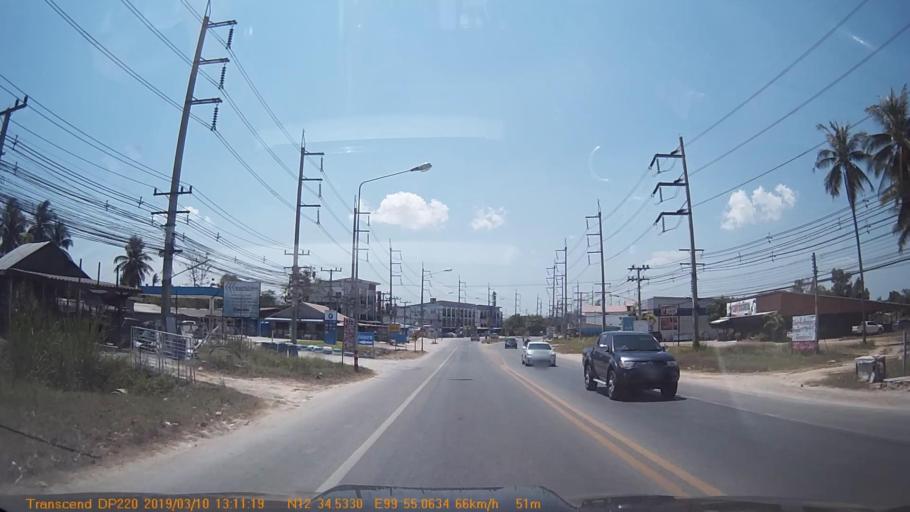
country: TH
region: Prachuap Khiri Khan
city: Hua Hin
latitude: 12.5755
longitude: 99.9176
